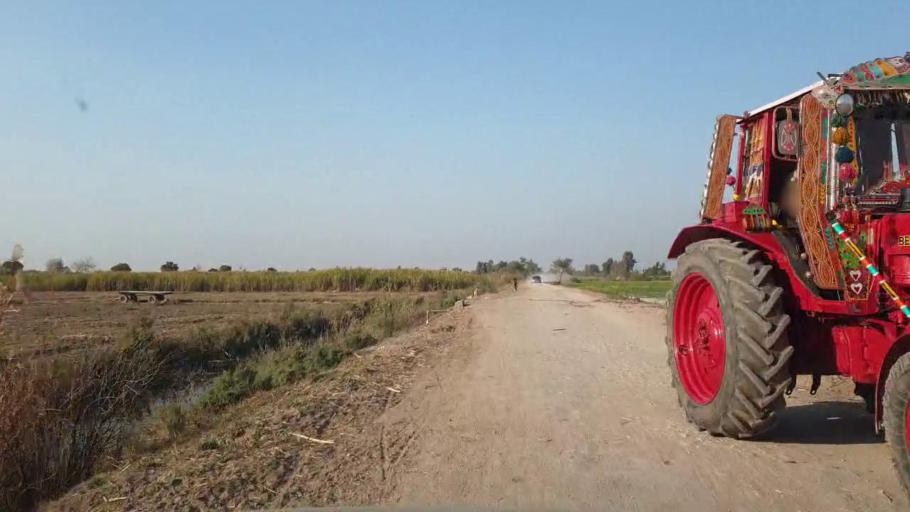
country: PK
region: Sindh
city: Tando Allahyar
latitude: 25.3467
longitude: 68.7058
